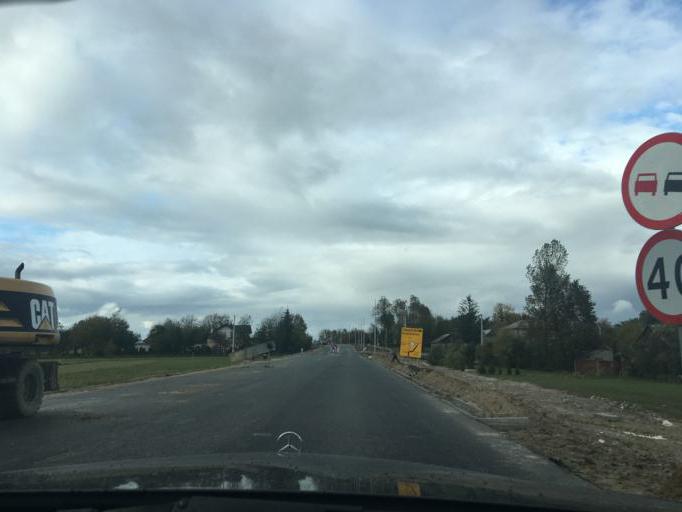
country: PL
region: Lublin Voivodeship
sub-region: Powiat lubelski
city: Krzczonow
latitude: 50.9779
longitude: 22.6814
